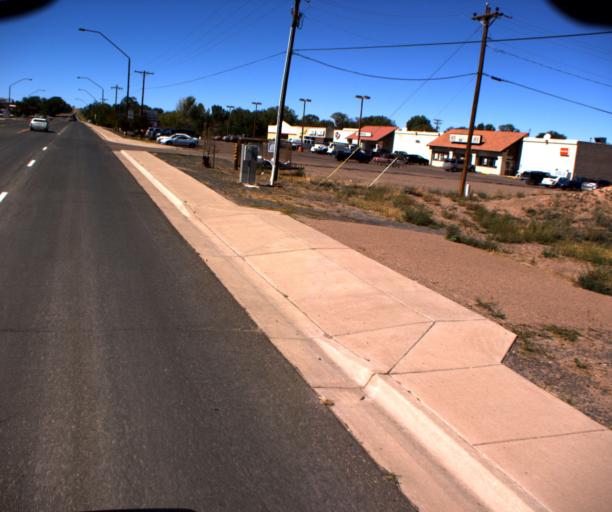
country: US
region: Arizona
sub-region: Apache County
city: Saint Johns
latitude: 34.5066
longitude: -109.3805
